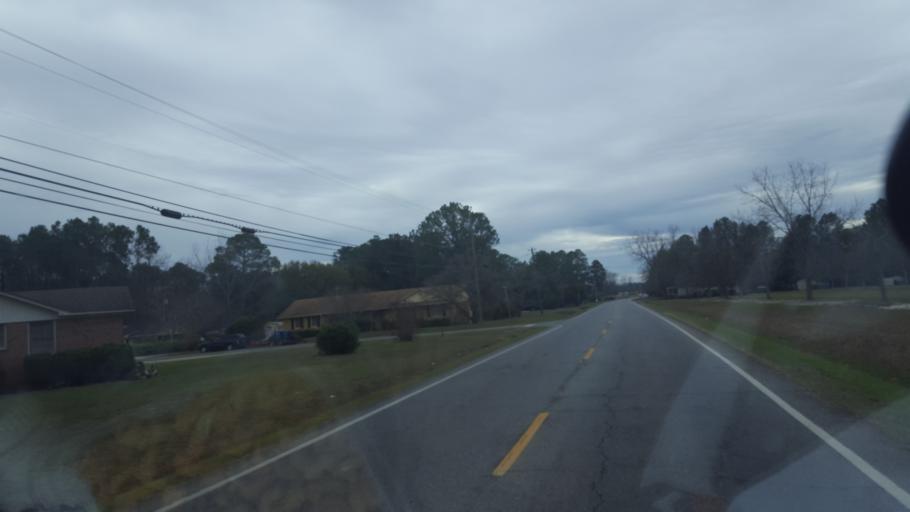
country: US
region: Georgia
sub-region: Ben Hill County
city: Fitzgerald
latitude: 31.7386
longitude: -83.2610
